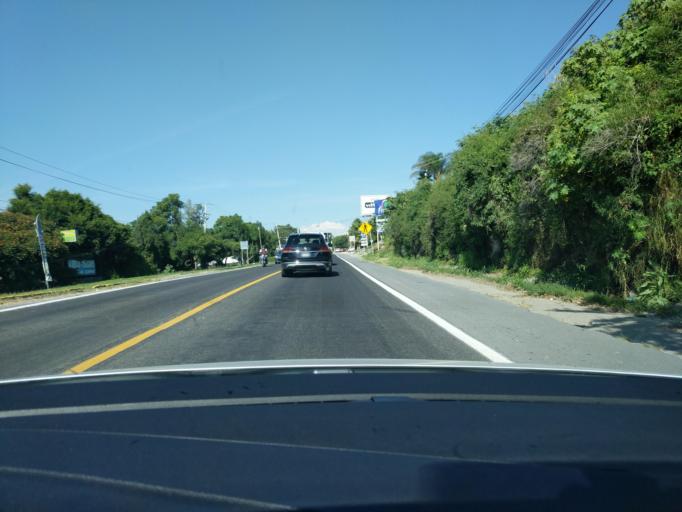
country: MX
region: Puebla
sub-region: Atlixco
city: San Agustin Huixaxtla
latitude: 18.9313
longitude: -98.4066
